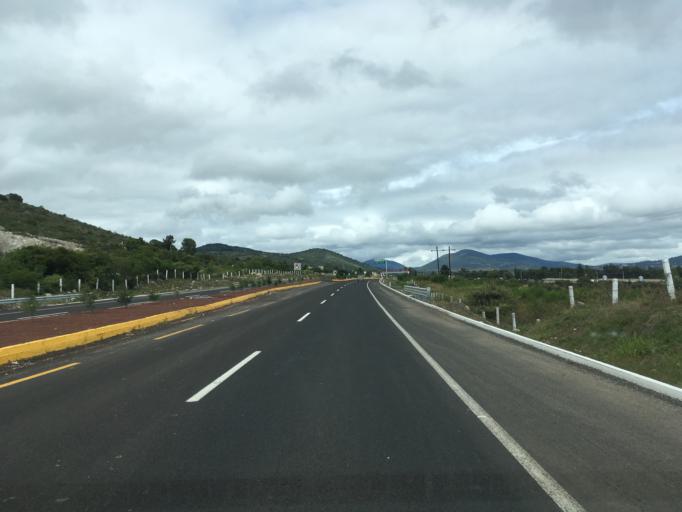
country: MX
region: Hidalgo
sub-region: Atotonilco el Grande
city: Santa Maria Amajac
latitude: 20.3365
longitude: -98.7055
